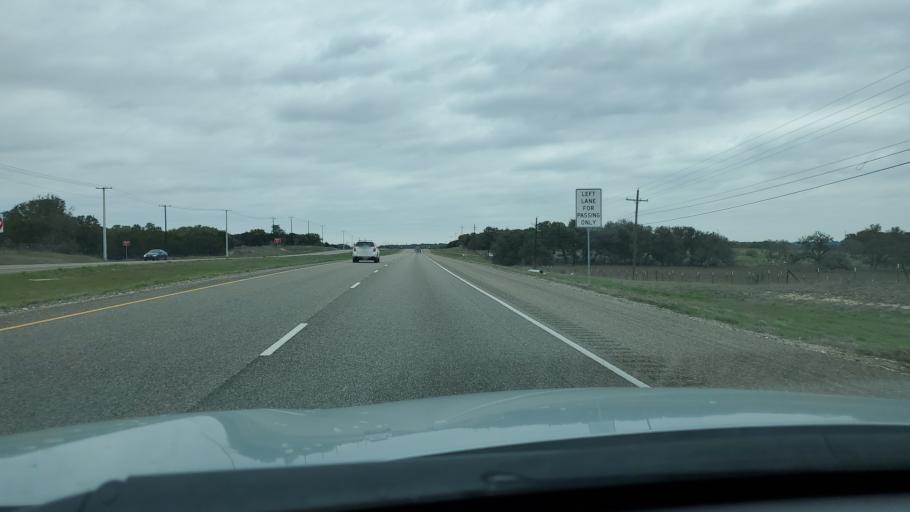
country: US
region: Texas
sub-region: Williamson County
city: Florence
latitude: 30.7941
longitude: -97.7669
